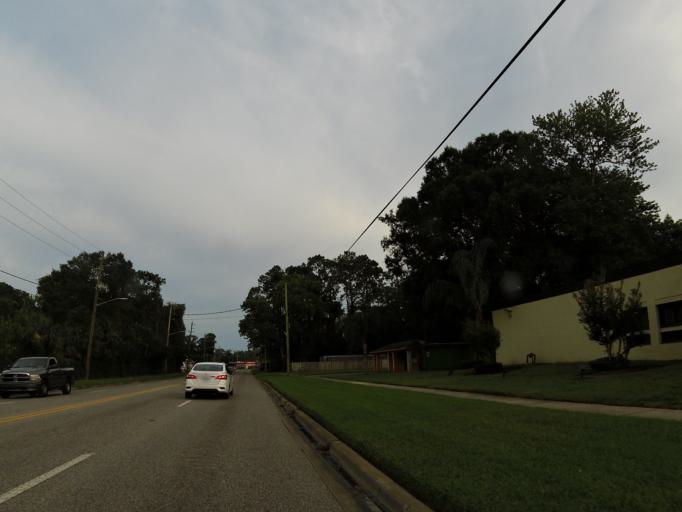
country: US
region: Florida
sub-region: Duval County
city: Jacksonville
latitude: 30.3747
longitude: -81.6898
